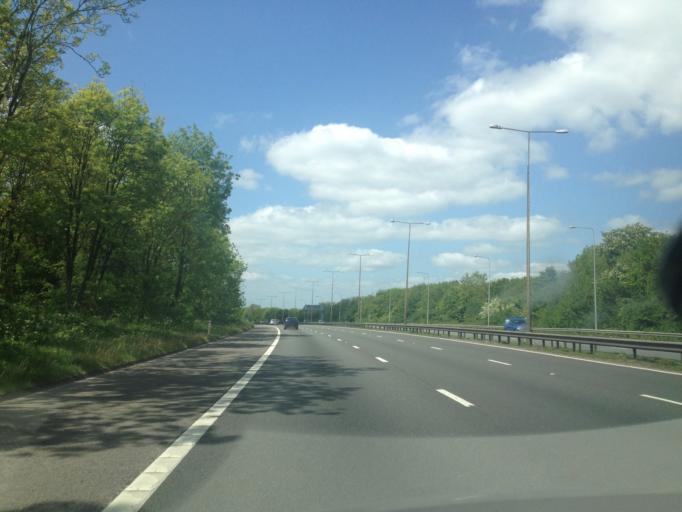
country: GB
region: England
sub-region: Hertfordshire
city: Elstree
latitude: 51.6438
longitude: -0.3252
